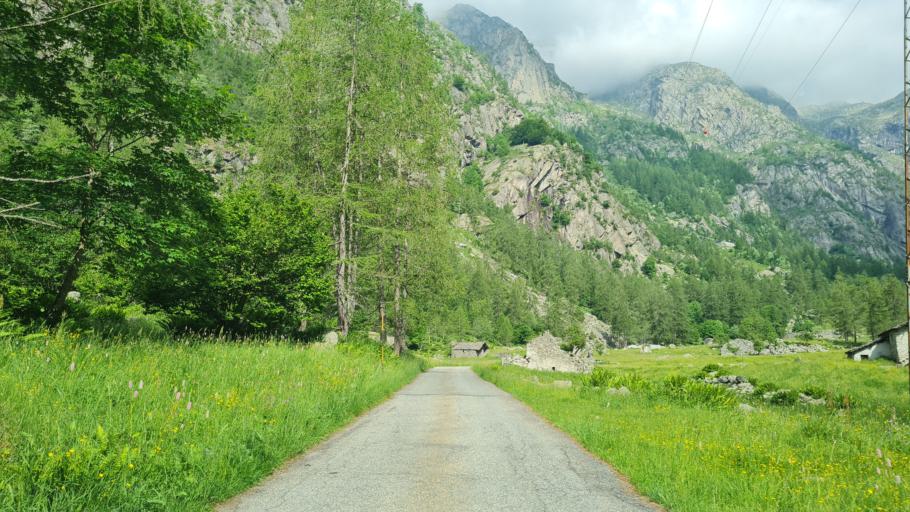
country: IT
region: Piedmont
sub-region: Provincia di Torino
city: Noasca
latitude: 45.4589
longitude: 7.3821
